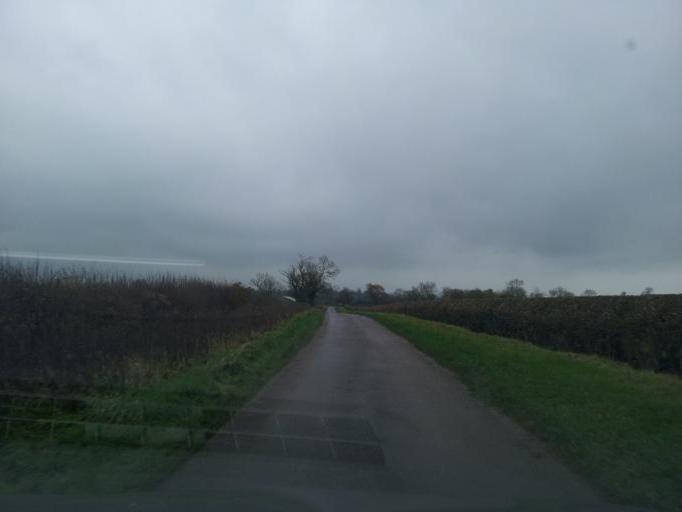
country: GB
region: England
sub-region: Warwickshire
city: Rugby
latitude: 52.3458
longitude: -1.1885
